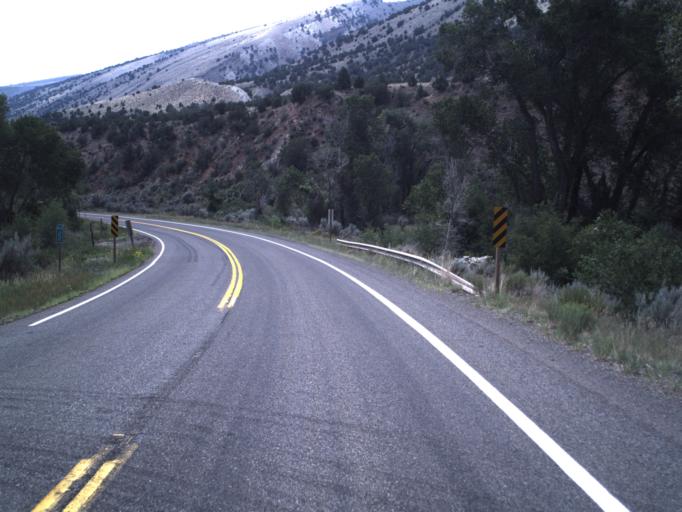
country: US
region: Utah
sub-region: Daggett County
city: Manila
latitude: 40.9282
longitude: -109.7211
